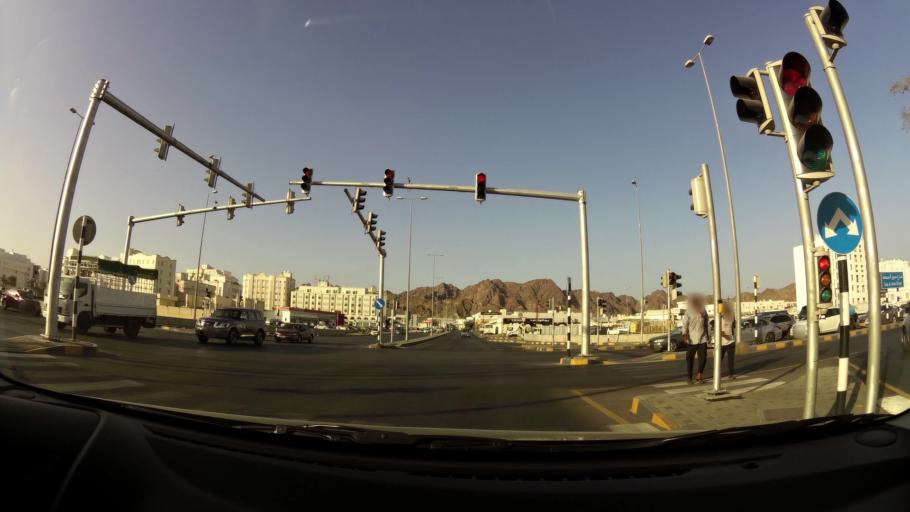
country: OM
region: Muhafazat Masqat
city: Muscat
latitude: 23.5882
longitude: 58.5521
